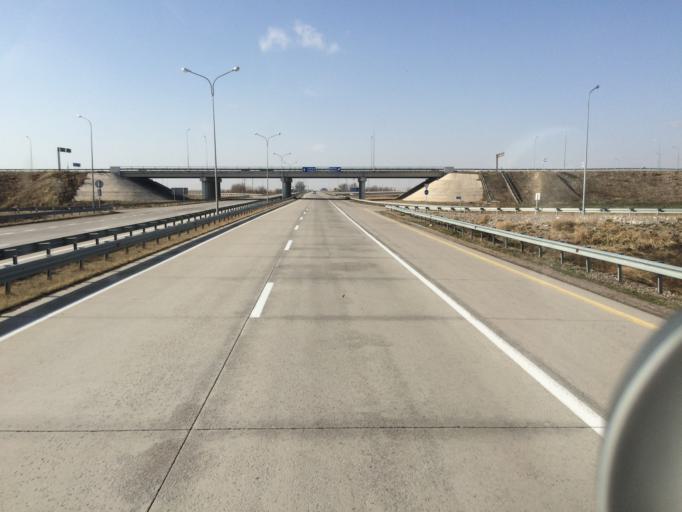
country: KZ
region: Zhambyl
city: Oytal
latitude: 42.9285
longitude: 73.2444
